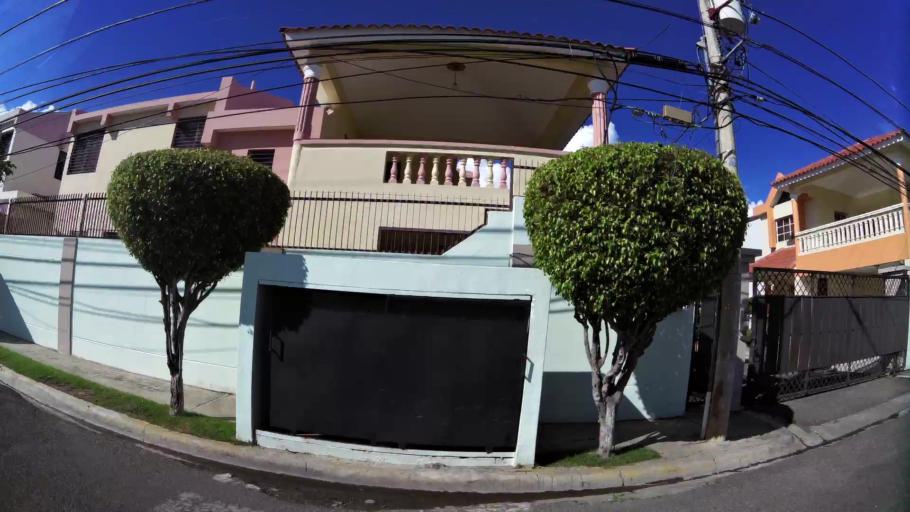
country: DO
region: Santiago
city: Santiago de los Caballeros
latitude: 19.4494
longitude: -70.6755
